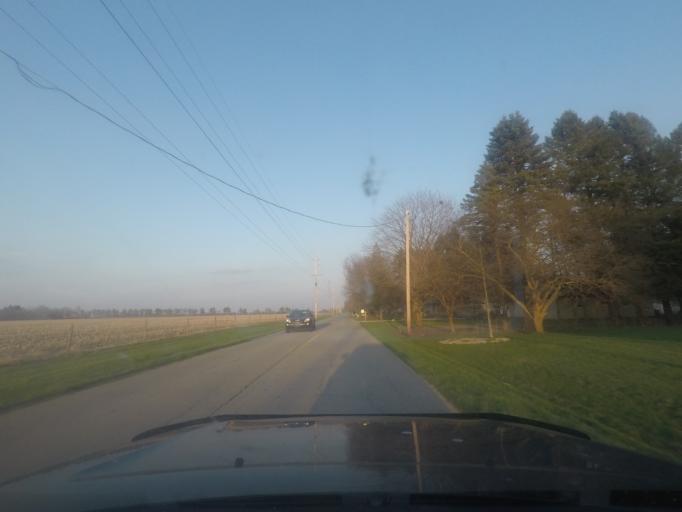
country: US
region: Indiana
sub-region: LaPorte County
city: LaPorte
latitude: 41.5692
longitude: -86.7077
